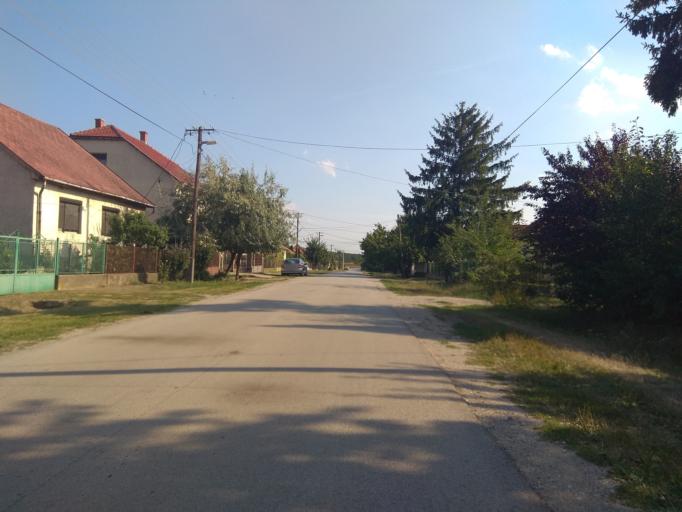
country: HU
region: Borsod-Abauj-Zemplen
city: Mezokeresztes
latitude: 47.8805
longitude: 20.6852
